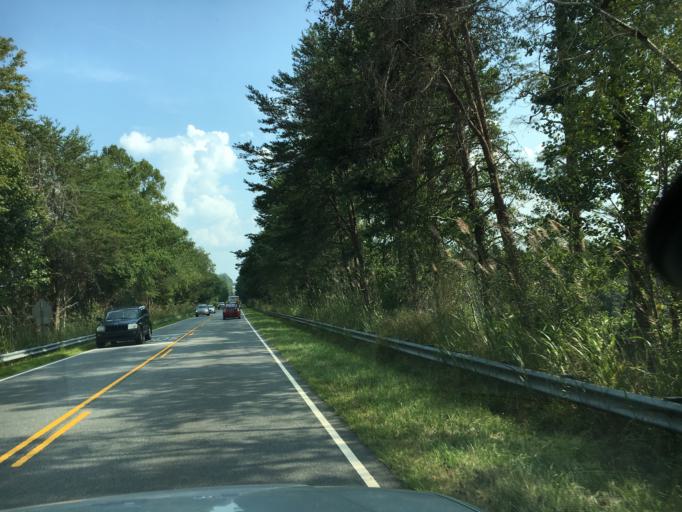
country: US
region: North Carolina
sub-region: Rutherford County
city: Rutherfordton
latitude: 35.3981
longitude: -81.9636
